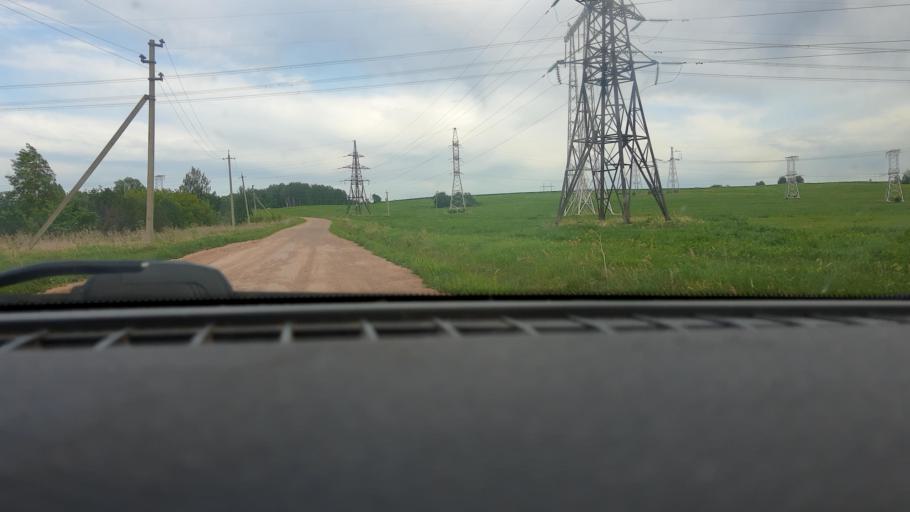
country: RU
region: Bashkortostan
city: Avdon
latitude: 54.4299
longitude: 55.8358
